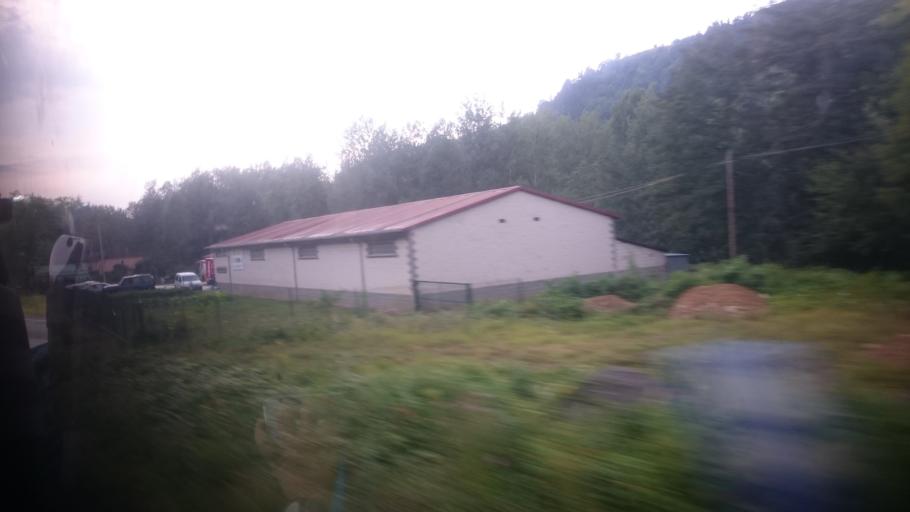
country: ES
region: Asturias
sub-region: Province of Asturias
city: Cangas de Onis
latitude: 43.3499
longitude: -5.0992
